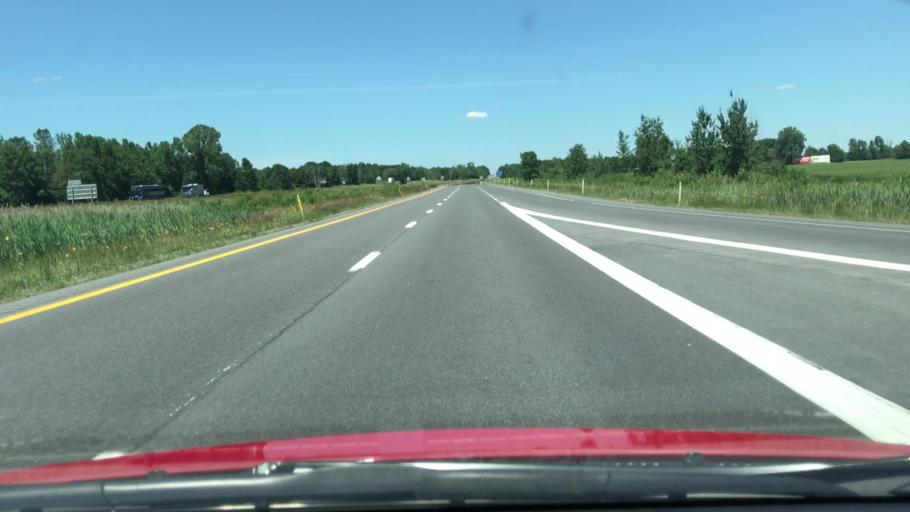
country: US
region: New York
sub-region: Clinton County
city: Cumberland Head
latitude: 44.7830
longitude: -73.4377
